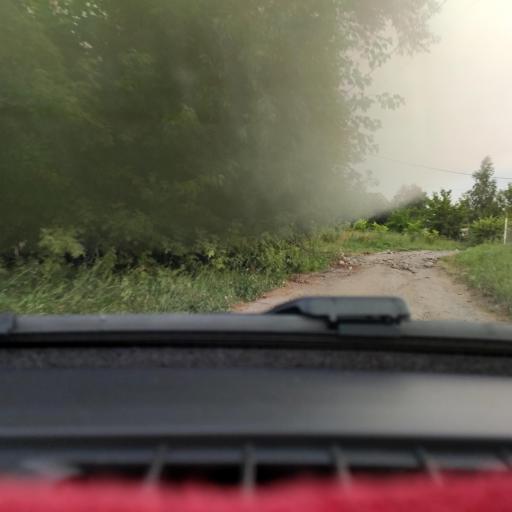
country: RU
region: Voronezj
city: Novaya Usman'
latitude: 51.6269
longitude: 39.3828
